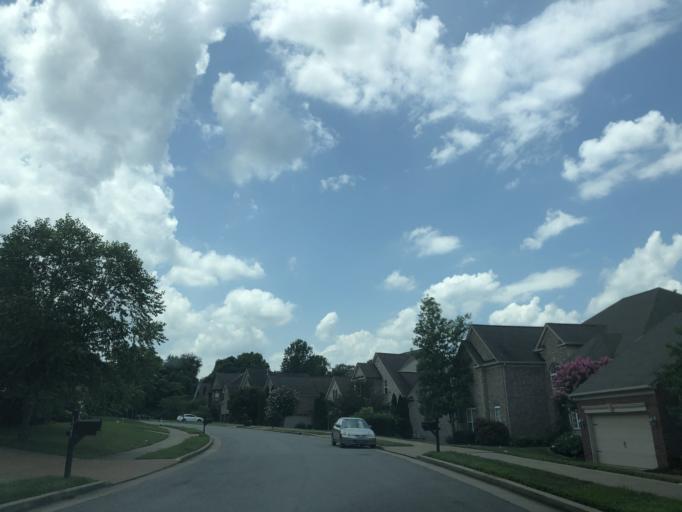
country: US
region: Tennessee
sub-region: Williamson County
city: Brentwood Estates
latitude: 36.0120
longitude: -86.7330
